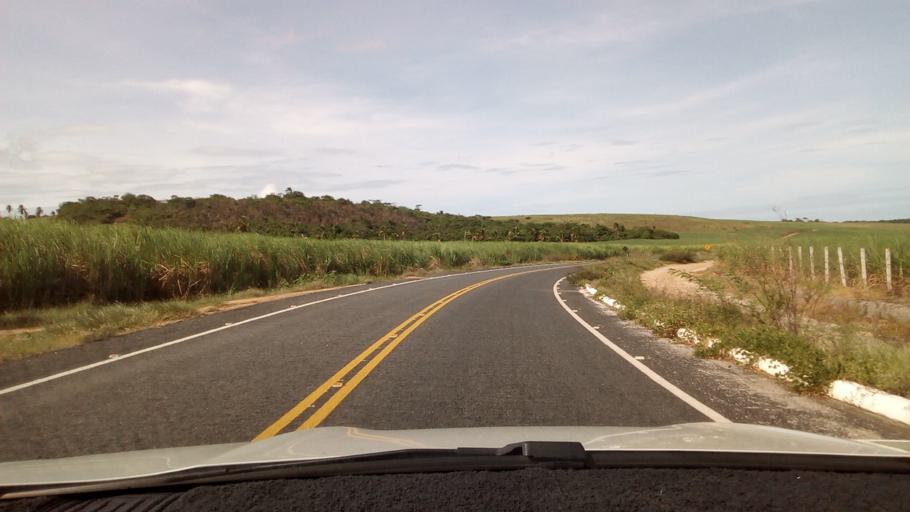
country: BR
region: Paraiba
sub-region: Joao Pessoa
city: Joao Pessoa
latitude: -7.0488
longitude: -34.8951
